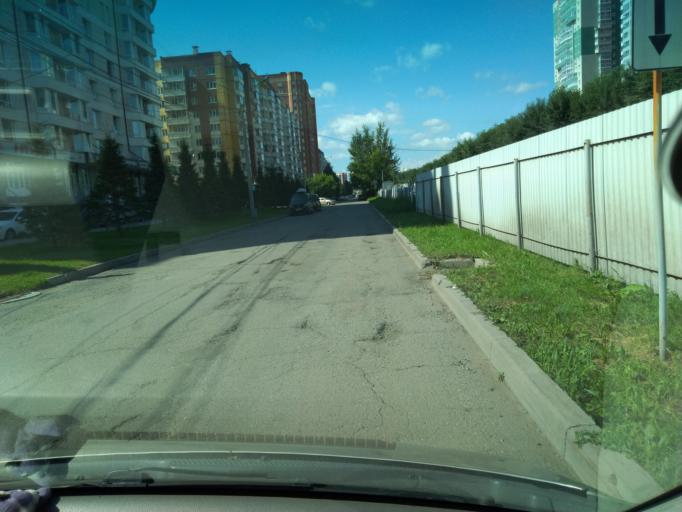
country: RU
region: Krasnoyarskiy
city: Krasnoyarsk
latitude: 56.0458
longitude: 92.9026
